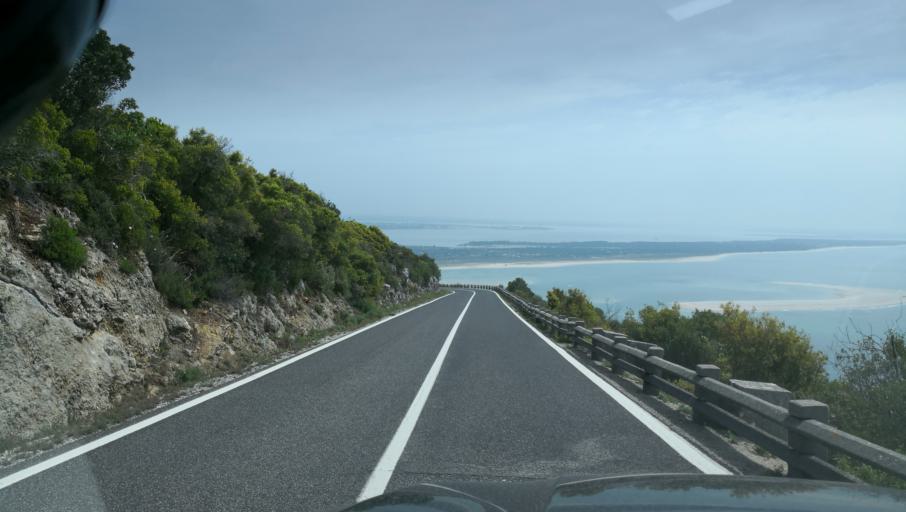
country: PT
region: Setubal
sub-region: Setubal
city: Setubal
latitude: 38.4879
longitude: -8.9451
